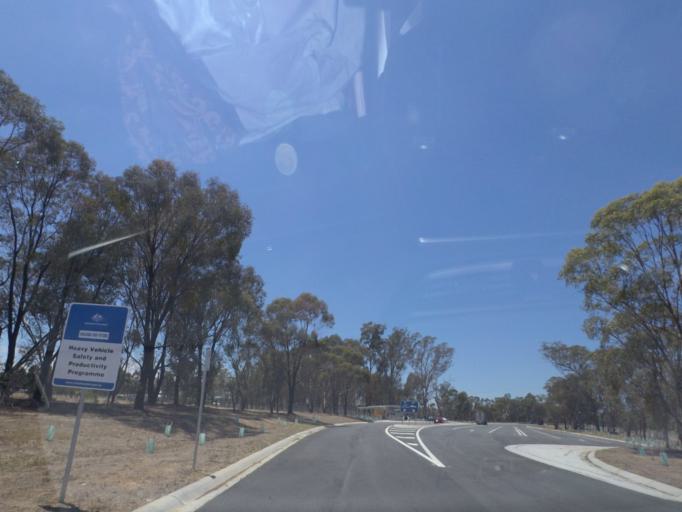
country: AU
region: Victoria
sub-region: Benalla
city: Benalla
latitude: -36.5756
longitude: 145.9289
